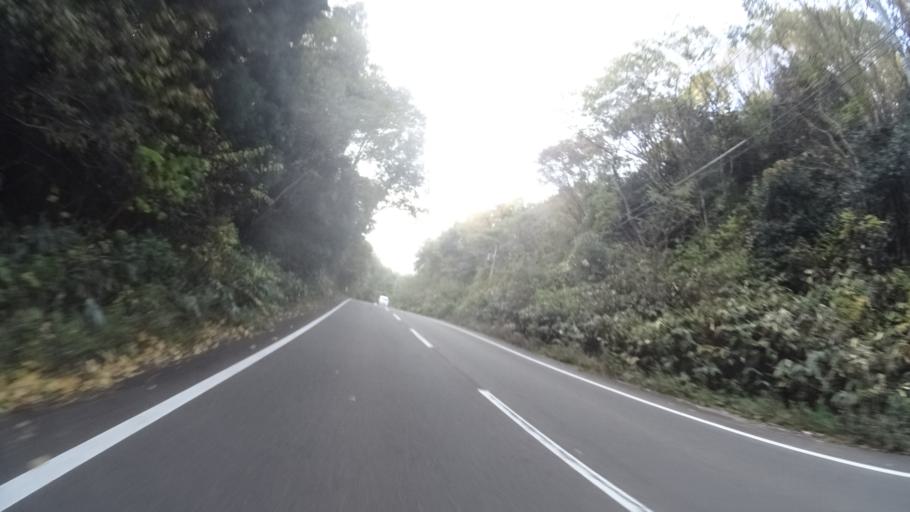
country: JP
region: Ishikawa
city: Nanao
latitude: 37.2054
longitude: 136.7089
